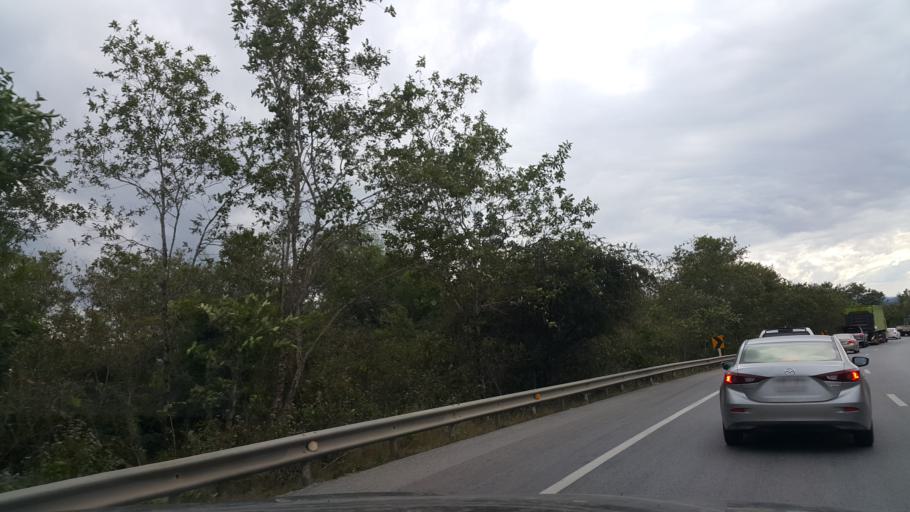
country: TH
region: Lampang
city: Sop Prap
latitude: 17.9740
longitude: 99.3559
